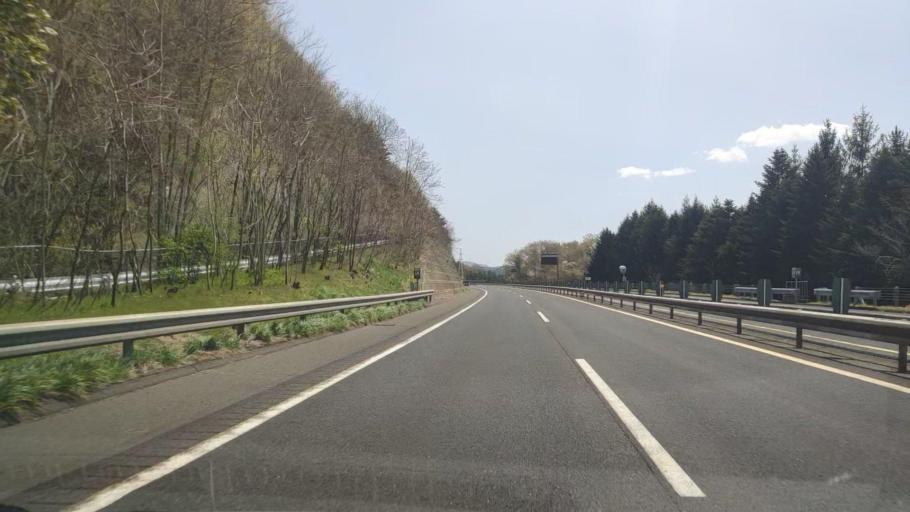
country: JP
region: Iwate
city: Ichinohe
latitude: 40.2320
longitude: 141.3036
